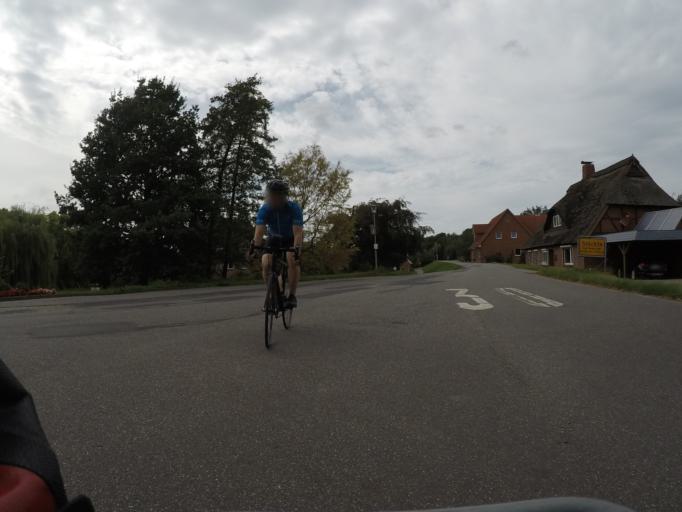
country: DE
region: Lower Saxony
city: Winsen
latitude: 53.3842
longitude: 10.2018
